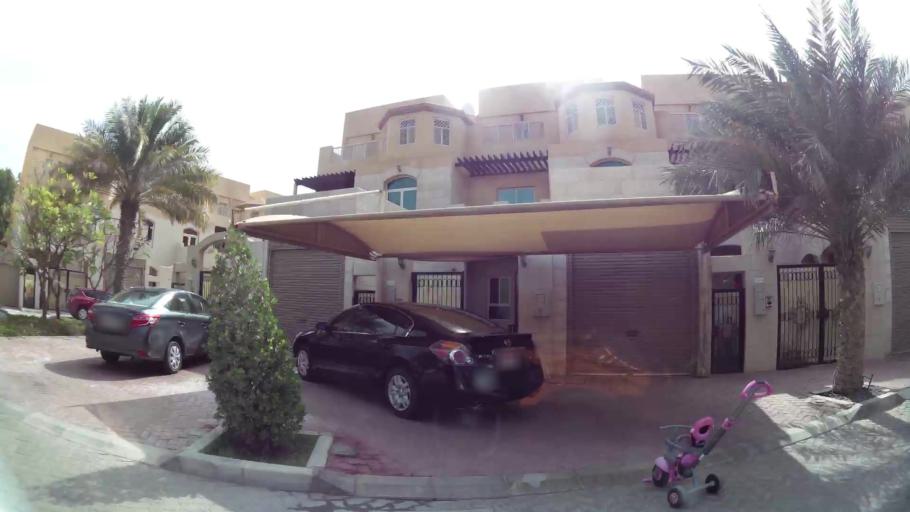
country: AE
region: Abu Dhabi
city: Abu Dhabi
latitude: 24.4437
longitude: 54.3719
